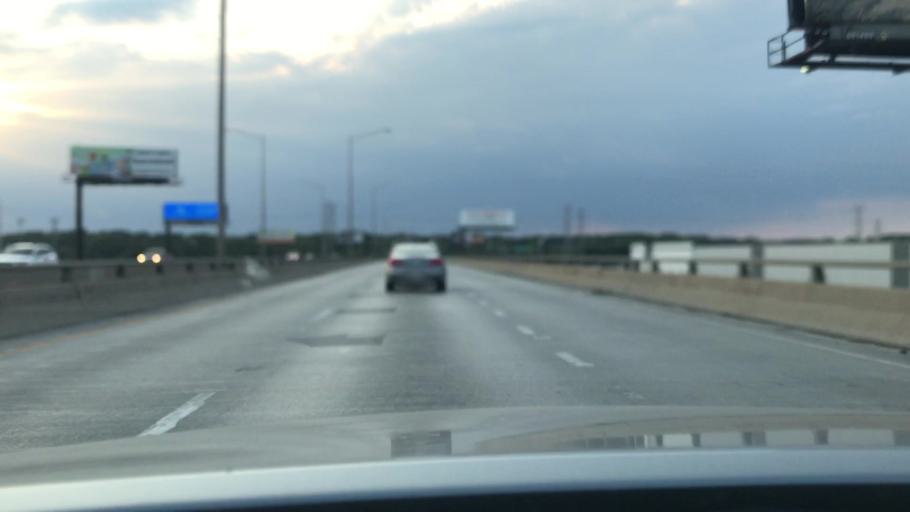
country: US
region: Illinois
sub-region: Cook County
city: Willow Springs
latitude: 41.7548
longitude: -87.8634
